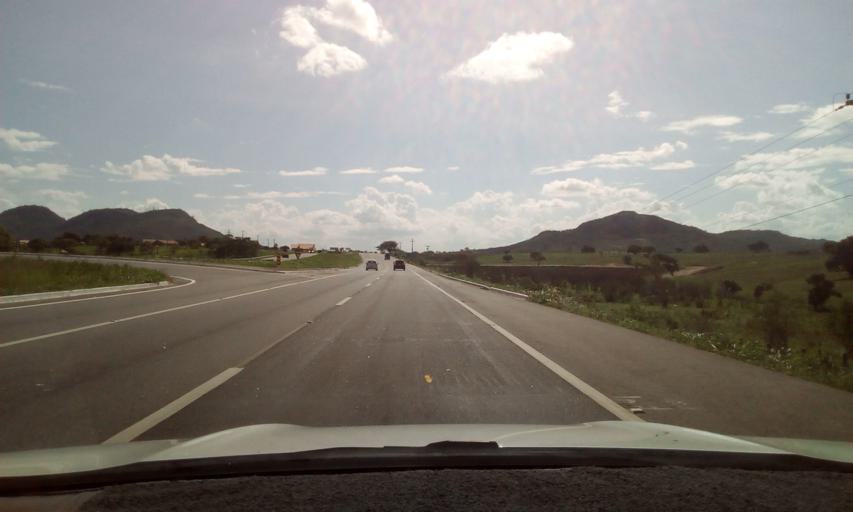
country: BR
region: Paraiba
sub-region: Gurinhem
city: Gurinhem
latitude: -7.1690
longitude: -35.3758
